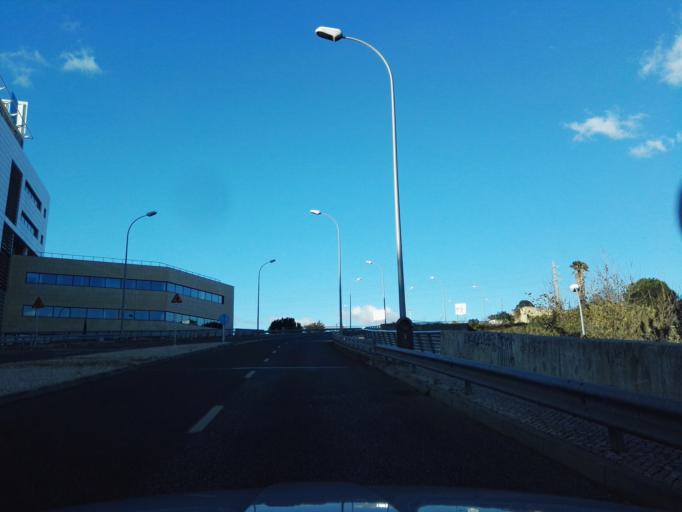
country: PT
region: Lisbon
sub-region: Oeiras
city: Alges
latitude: 38.7150
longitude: -9.2244
